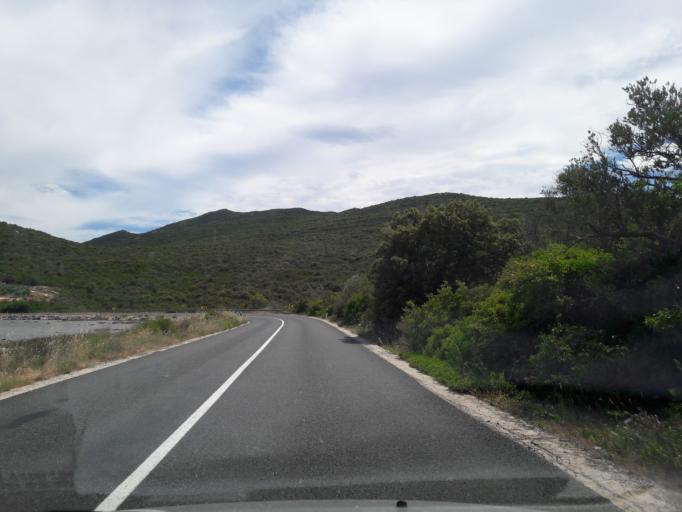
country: HR
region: Dubrovacko-Neretvanska
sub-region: Grad Dubrovnik
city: Opuzen
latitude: 42.9157
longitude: 17.4679
